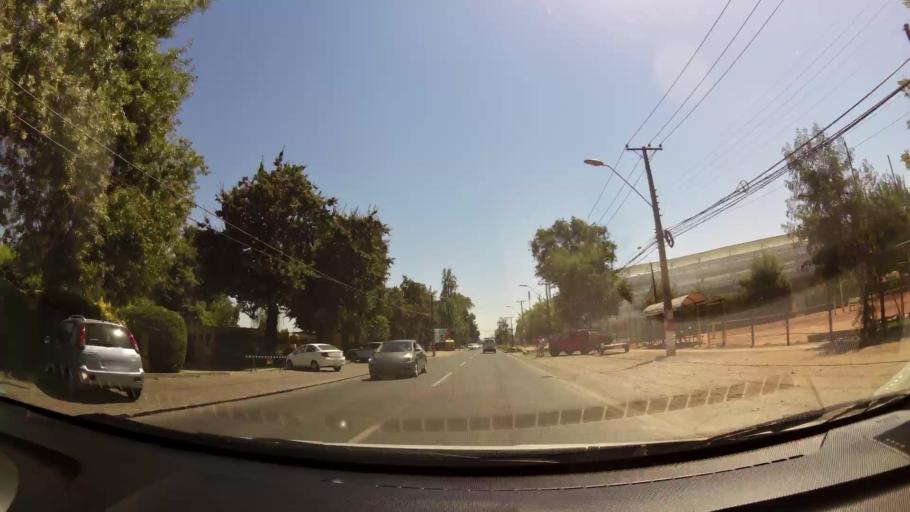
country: CL
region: Maule
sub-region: Provincia de Curico
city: Curico
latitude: -34.9757
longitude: -71.2321
